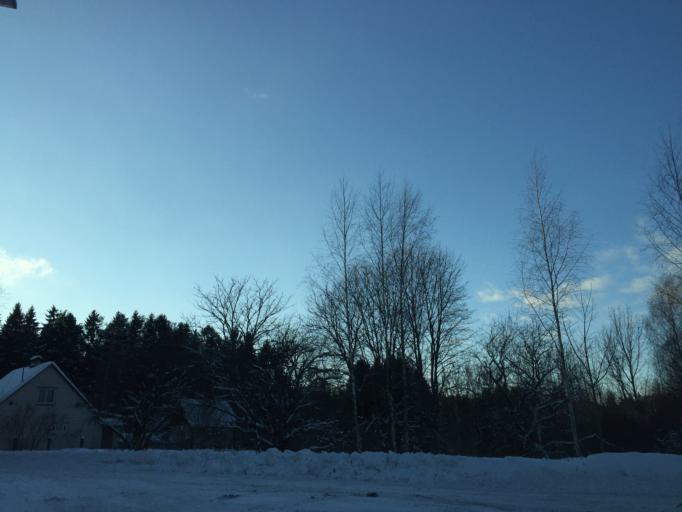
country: LV
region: Incukalns
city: Incukalns
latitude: 57.1037
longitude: 24.6755
